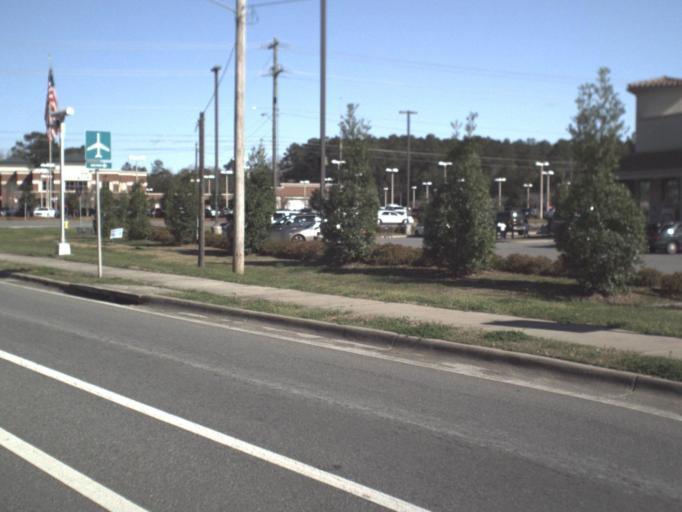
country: US
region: Florida
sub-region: Leon County
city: Tallahassee
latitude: 30.4584
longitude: -84.3621
